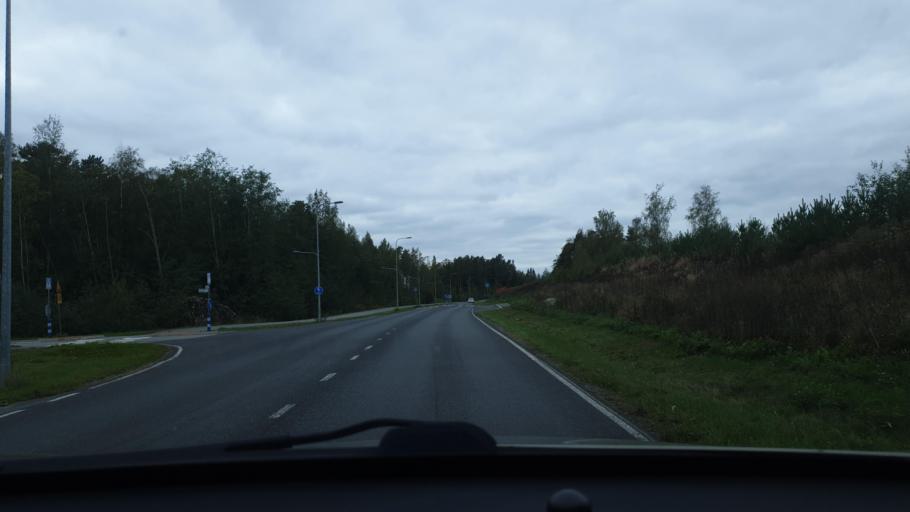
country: FI
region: Ostrobothnia
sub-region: Vaasa
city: Teeriniemi
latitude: 63.1018
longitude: 21.6865
